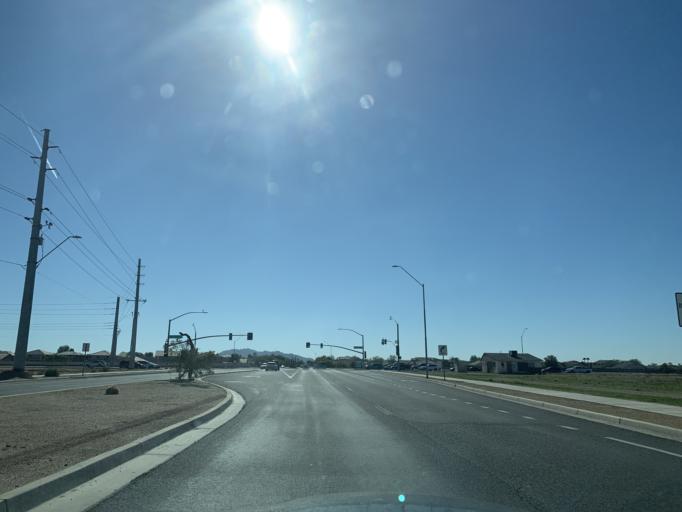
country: US
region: Arizona
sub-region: Pinal County
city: Casa Grande
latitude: 32.8954
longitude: -111.7227
